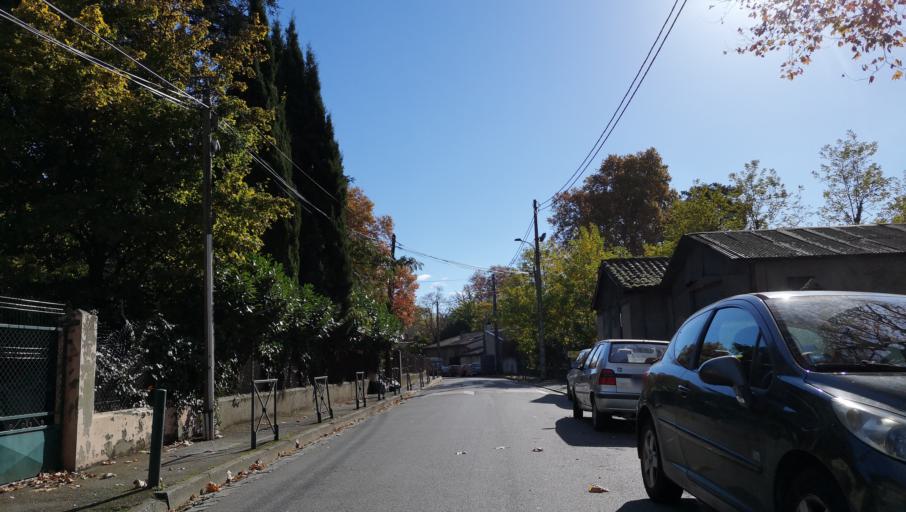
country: FR
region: Midi-Pyrenees
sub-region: Departement de la Haute-Garonne
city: Toulouse
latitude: 43.6092
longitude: 1.4157
